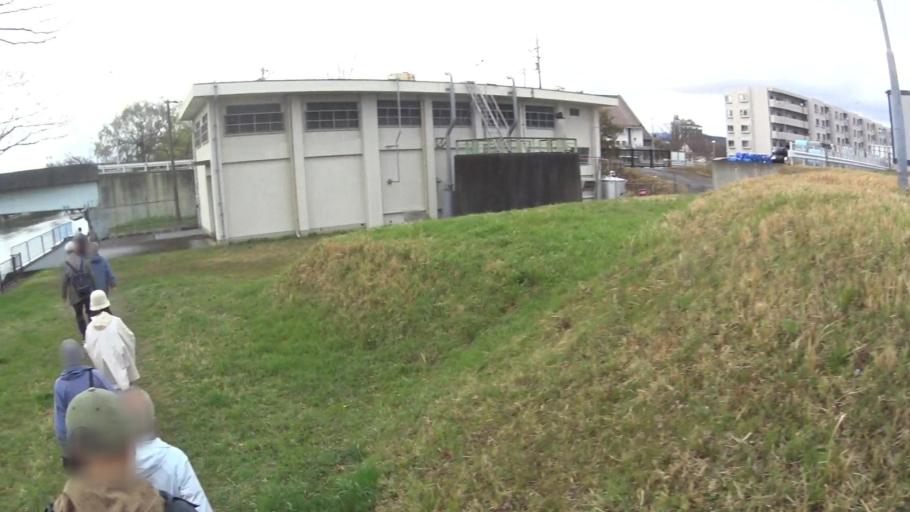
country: JP
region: Kyoto
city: Uji
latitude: 34.9236
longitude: 135.7572
